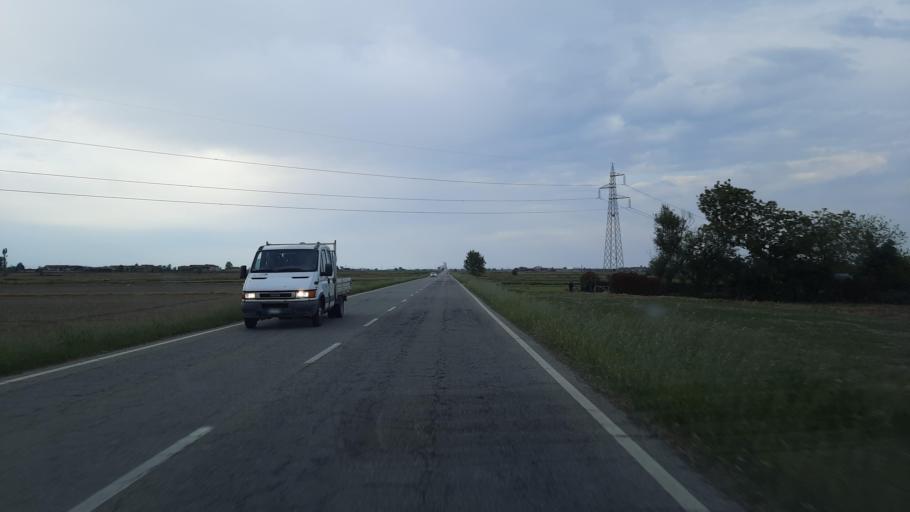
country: IT
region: Piedmont
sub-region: Provincia di Vercelli
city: Crescentino
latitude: 45.2051
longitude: 8.1172
